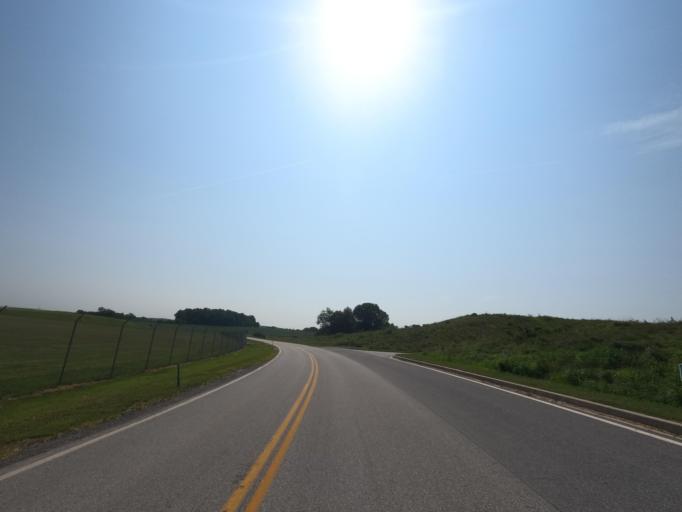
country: US
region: Maryland
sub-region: Carroll County
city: Westminster
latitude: 39.5990
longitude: -77.0027
